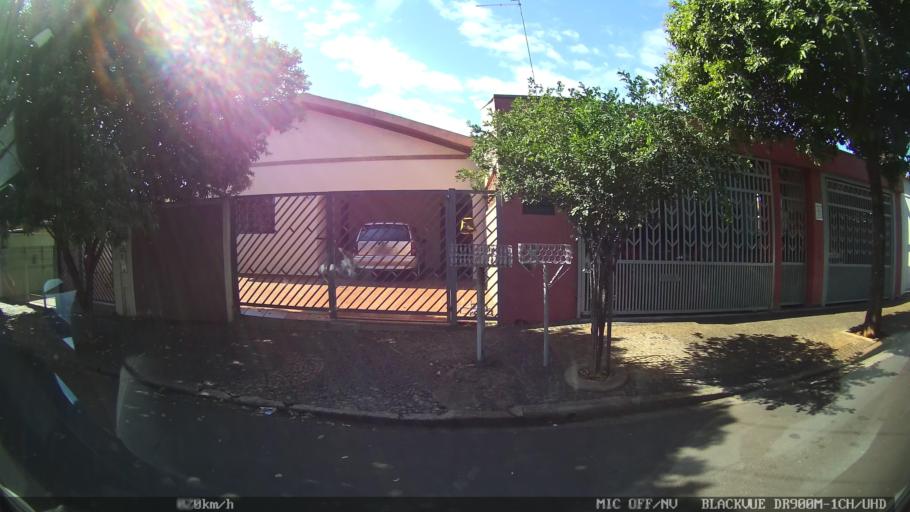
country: BR
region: Sao Paulo
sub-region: Americana
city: Americana
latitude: -22.7400
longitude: -47.3730
